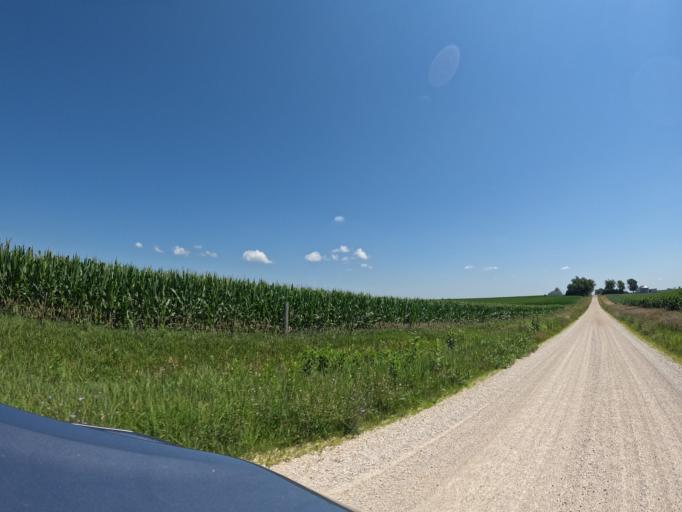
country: US
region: Iowa
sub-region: Clinton County
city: De Witt
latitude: 41.7720
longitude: -90.4051
